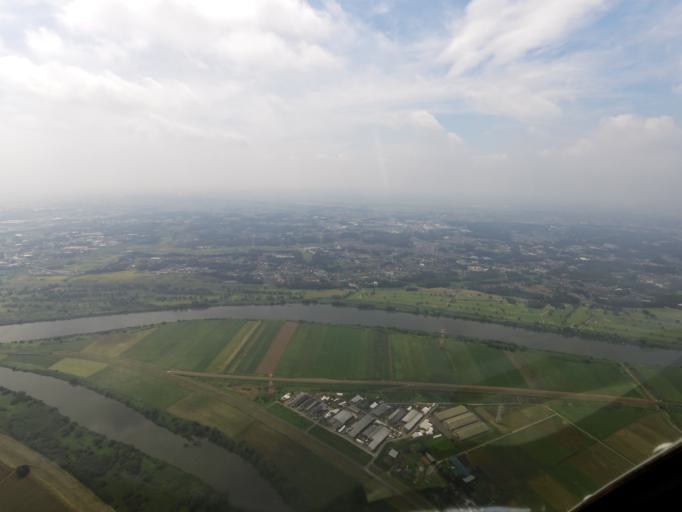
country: JP
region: Ibaraki
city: Moriya
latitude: 35.9518
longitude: 139.9470
